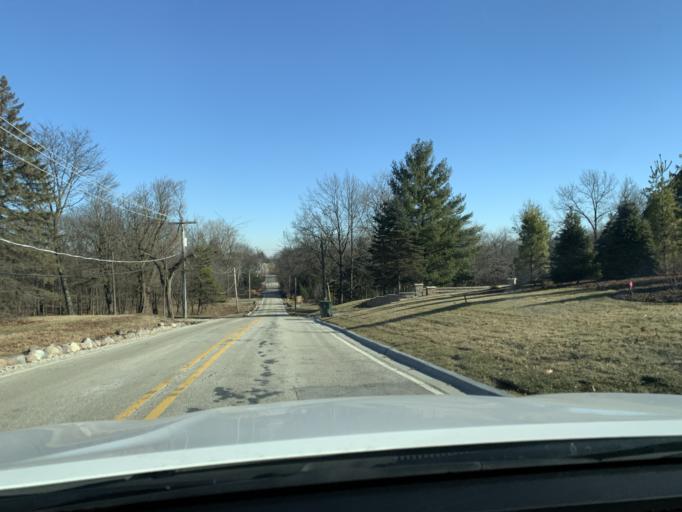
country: US
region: Illinois
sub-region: DuPage County
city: Burr Ridge
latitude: 41.7310
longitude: -87.9197
